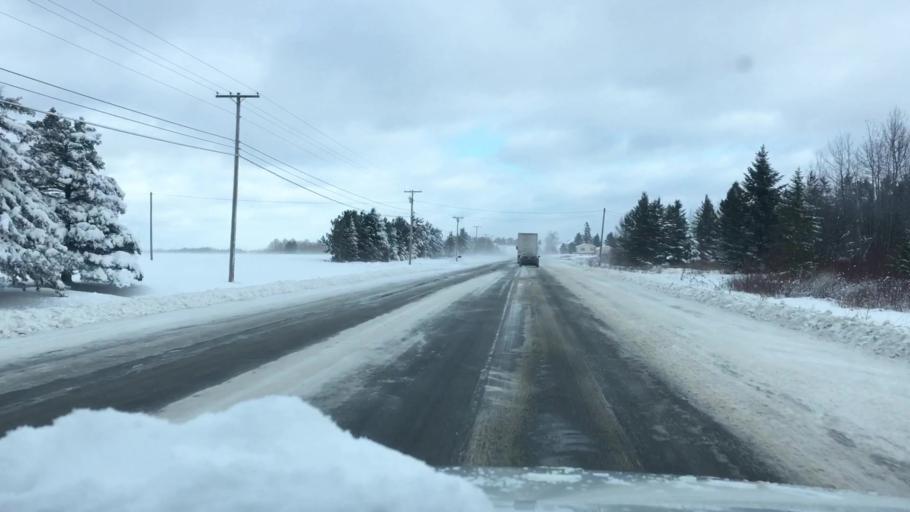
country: US
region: Maine
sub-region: Aroostook County
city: Presque Isle
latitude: 46.7377
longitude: -67.9986
